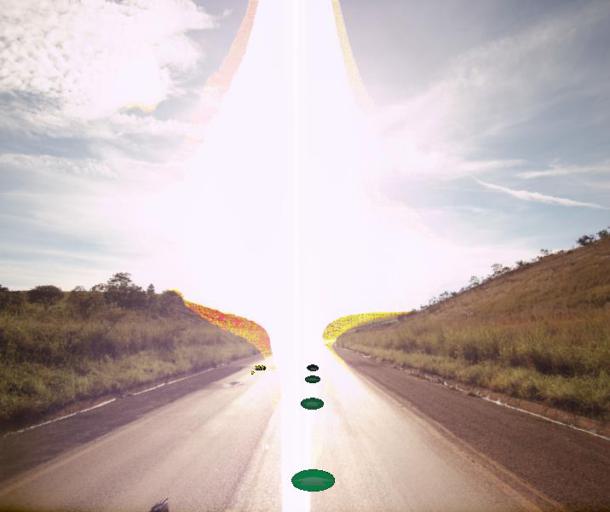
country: BR
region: Federal District
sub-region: Brasilia
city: Brasilia
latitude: -15.7540
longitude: -48.4274
